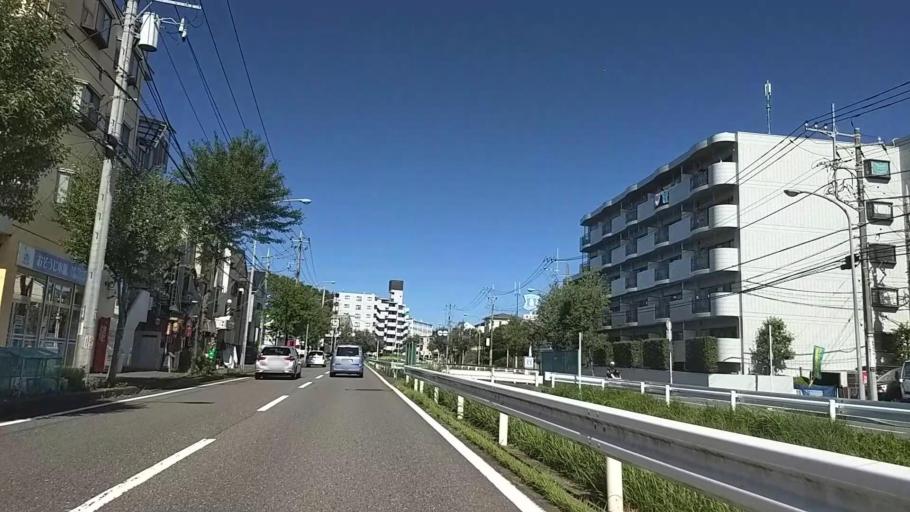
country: JP
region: Tokyo
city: Chofugaoka
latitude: 35.5818
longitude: 139.5459
